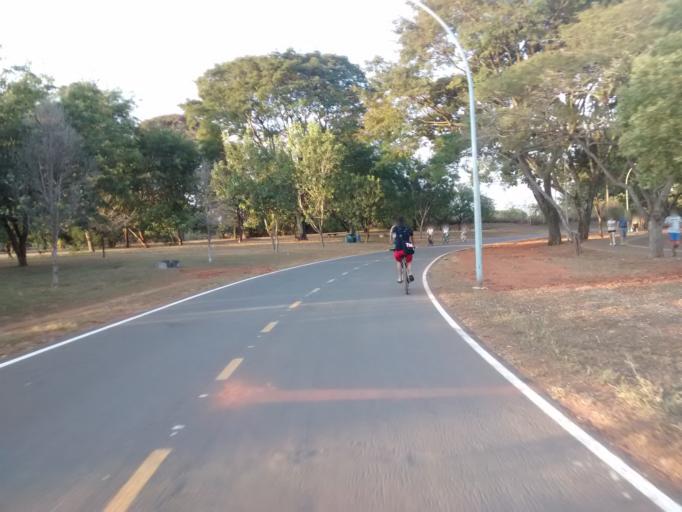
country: BR
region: Federal District
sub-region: Brasilia
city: Brasilia
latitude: -15.8034
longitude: -47.9105
